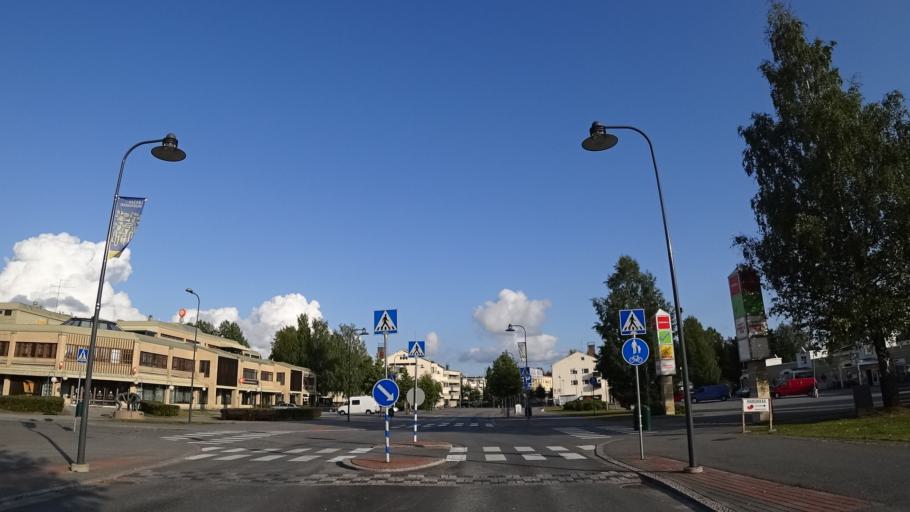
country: FI
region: North Karelia
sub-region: Pielisen Karjala
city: Lieksa
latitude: 63.3171
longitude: 30.0303
